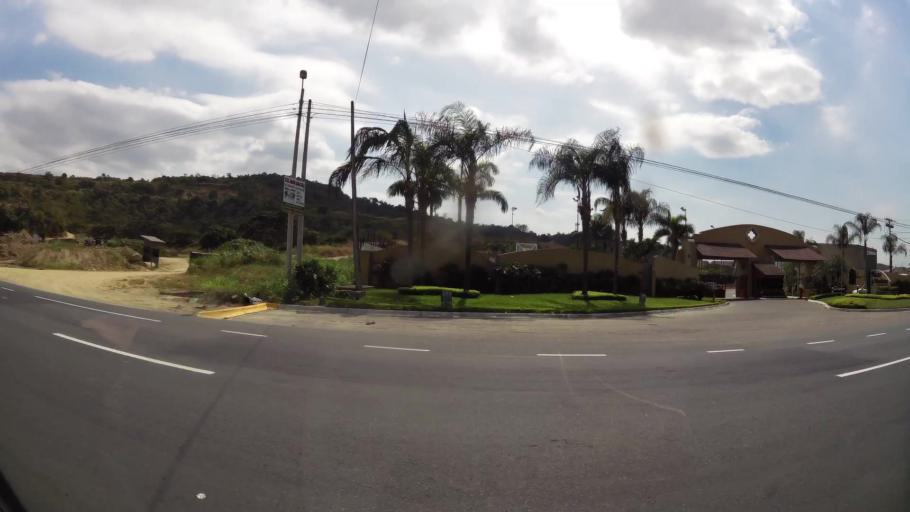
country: EC
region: Guayas
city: El Triunfo
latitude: -2.0542
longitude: -79.9164
